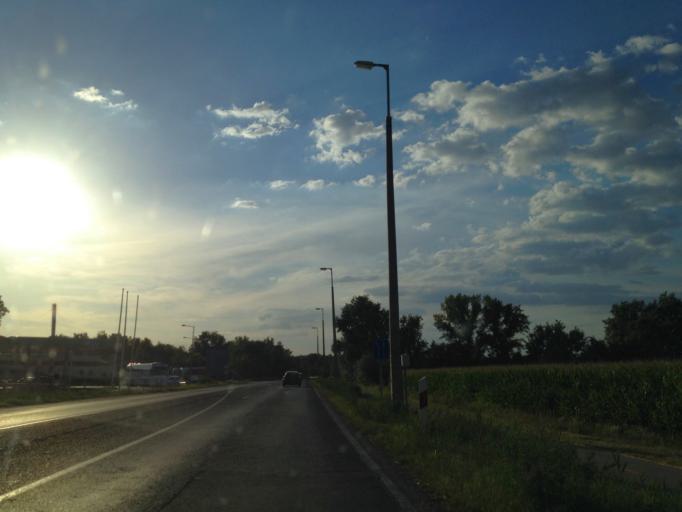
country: HU
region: Gyor-Moson-Sopron
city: Abda
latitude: 47.6833
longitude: 17.5703
